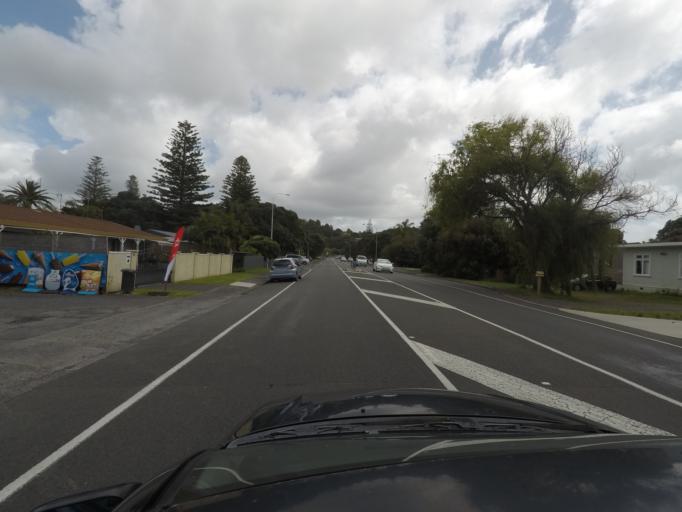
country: NZ
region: Auckland
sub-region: Auckland
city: Rothesay Bay
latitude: -36.5778
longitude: 174.6916
